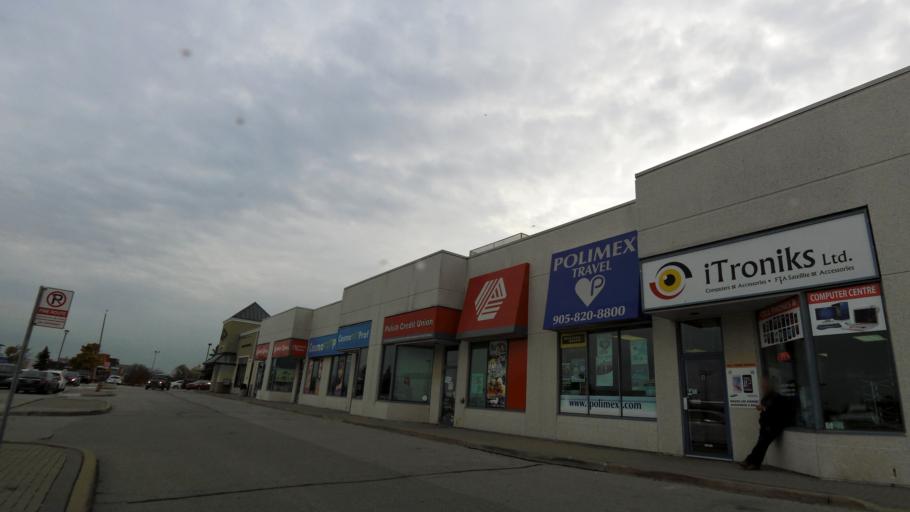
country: CA
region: Ontario
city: Mississauga
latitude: 43.5203
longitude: -79.6862
